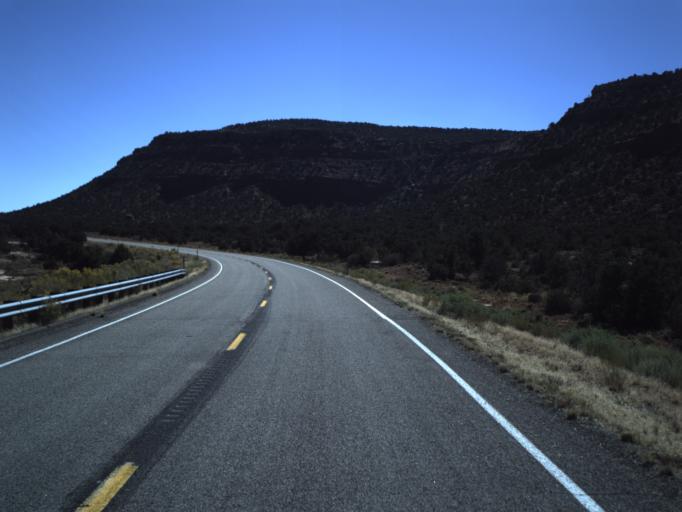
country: US
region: Utah
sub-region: San Juan County
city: Blanding
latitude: 37.6371
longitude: -110.1068
